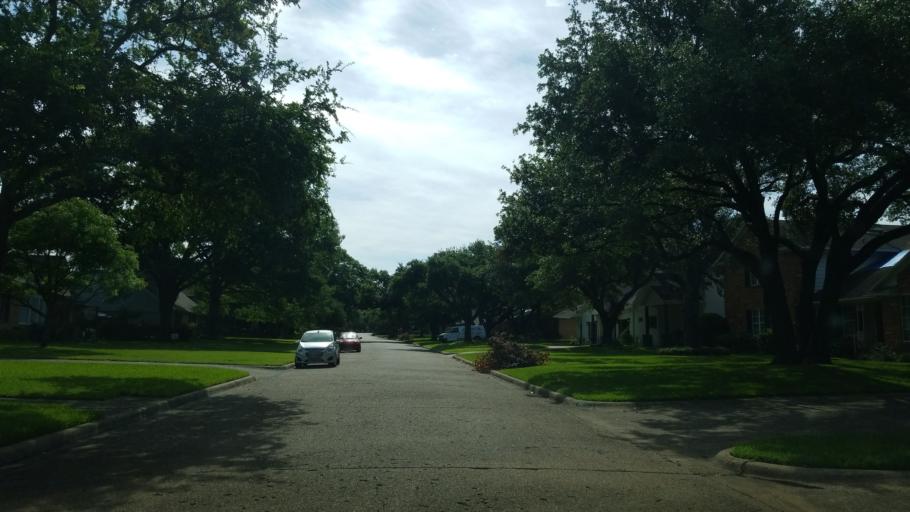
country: US
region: Texas
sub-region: Dallas County
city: Farmers Branch
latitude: 32.9031
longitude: -96.8415
